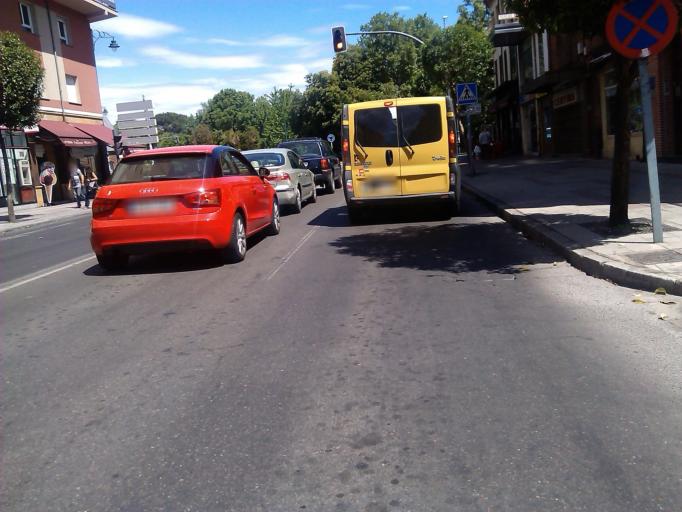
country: ES
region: Castille and Leon
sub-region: Provincia de Leon
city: Leon
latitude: 42.5997
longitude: -5.5857
